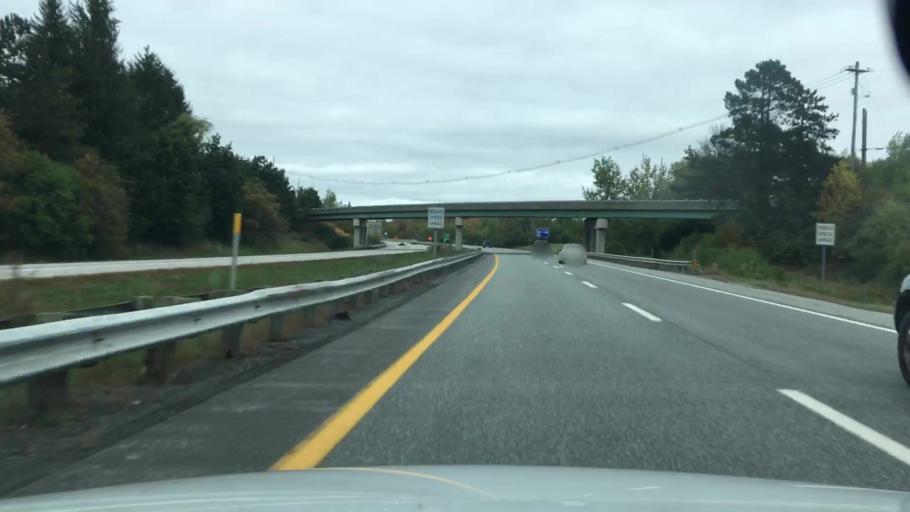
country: US
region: Maine
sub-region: Penobscot County
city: Hampden
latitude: 44.7803
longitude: -68.8191
